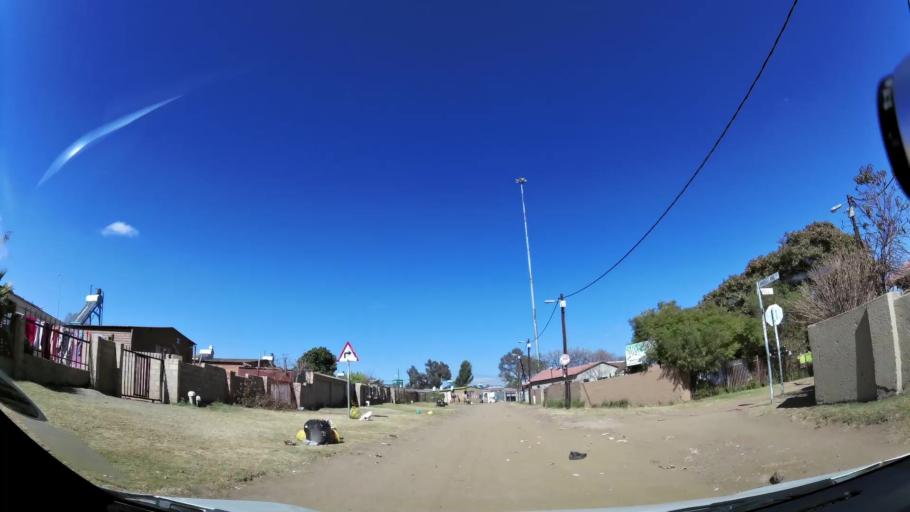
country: ZA
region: Gauteng
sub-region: City of Johannesburg Metropolitan Municipality
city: Midrand
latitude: -25.9218
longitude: 28.0982
